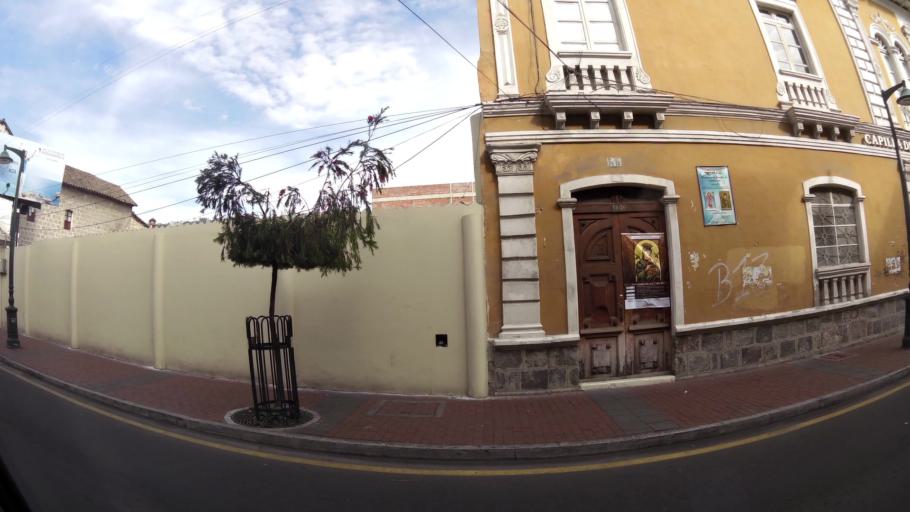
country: EC
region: Tungurahua
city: Ambato
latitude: -1.2375
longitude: -78.6297
